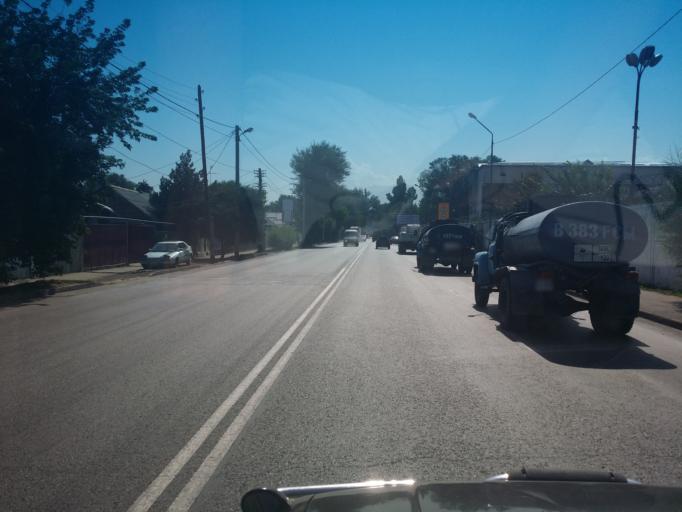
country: KZ
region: Almaty Oblysy
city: Pervomayskiy
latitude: 43.3523
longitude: 76.9566
